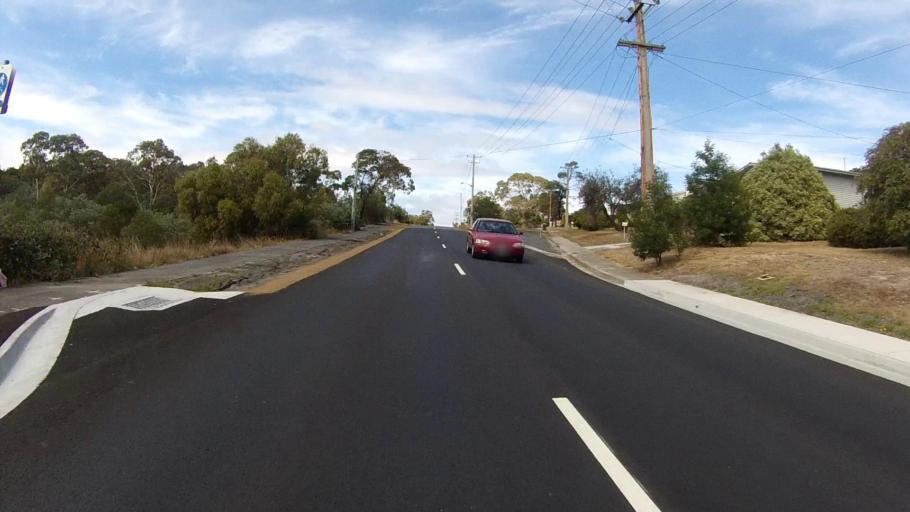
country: AU
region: Tasmania
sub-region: Clarence
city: Lindisfarne
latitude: -42.8148
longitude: 147.3513
